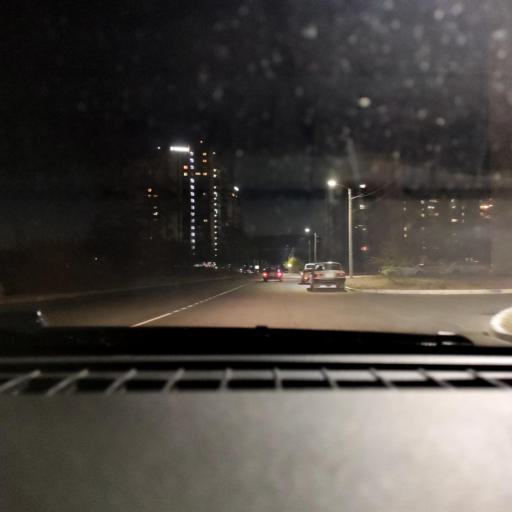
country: RU
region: Voronezj
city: Maslovka
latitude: 51.5892
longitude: 39.2478
